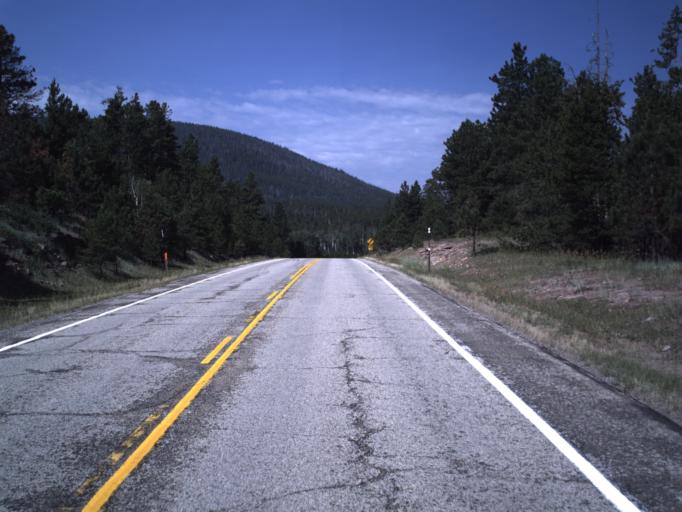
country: US
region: Utah
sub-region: Daggett County
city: Manila
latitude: 40.8502
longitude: -109.5815
